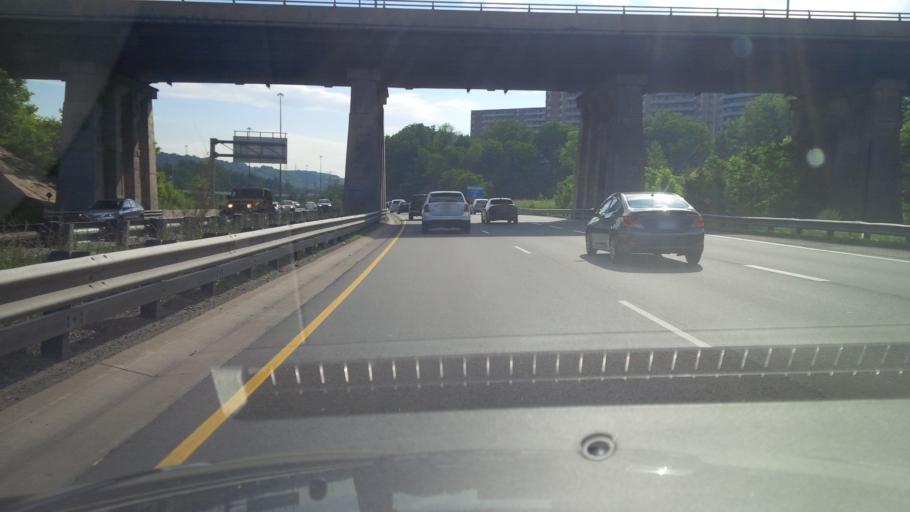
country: CA
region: Ontario
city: Hamilton
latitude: 43.2581
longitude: -79.9013
